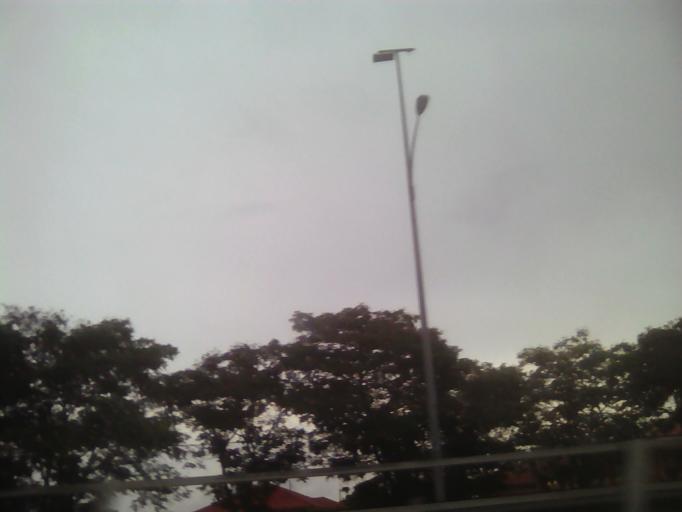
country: MY
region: Penang
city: Perai
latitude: 5.3993
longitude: 100.4085
